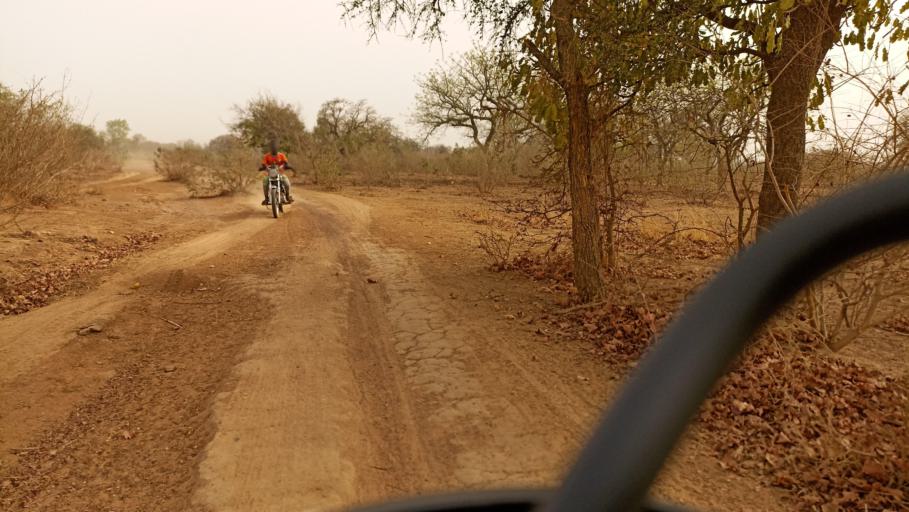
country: BF
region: Nord
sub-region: Province du Zondoma
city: Gourcy
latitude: 13.1597
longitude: -2.5934
